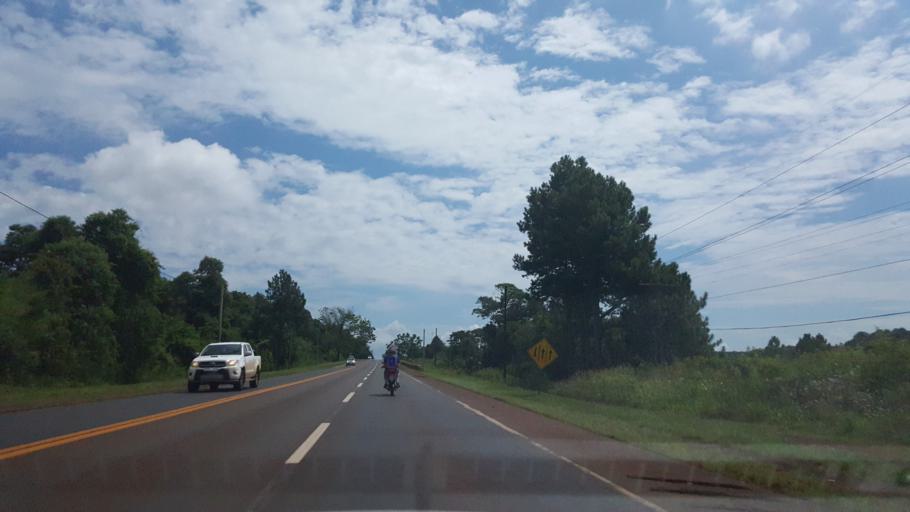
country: AR
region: Misiones
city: Capiovi
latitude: -26.9188
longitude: -55.0589
